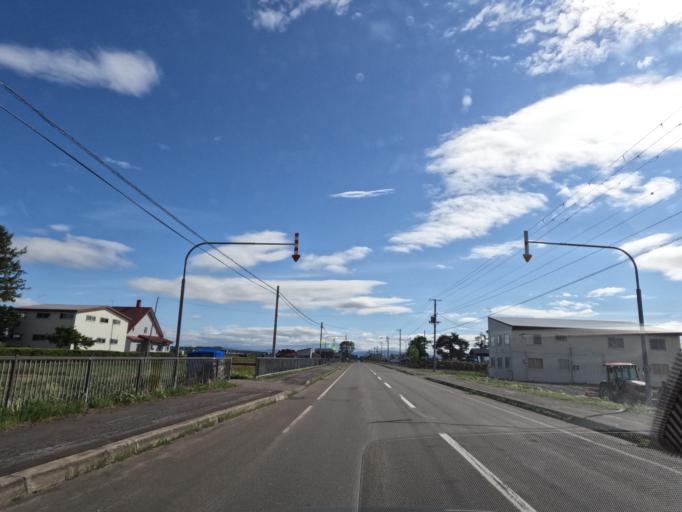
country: JP
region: Hokkaido
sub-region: Asahikawa-shi
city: Asahikawa
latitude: 43.7143
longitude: 142.5259
